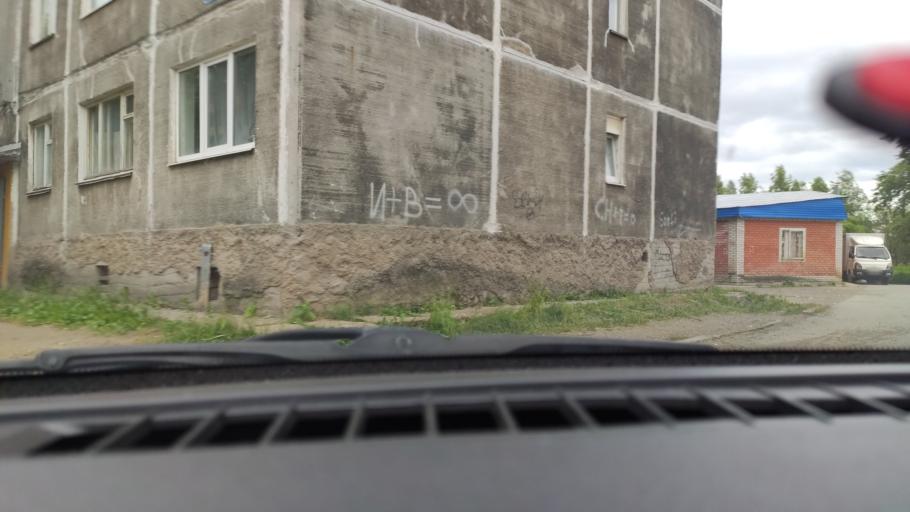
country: RU
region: Perm
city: Dobryanka
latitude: 58.4666
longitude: 56.3919
